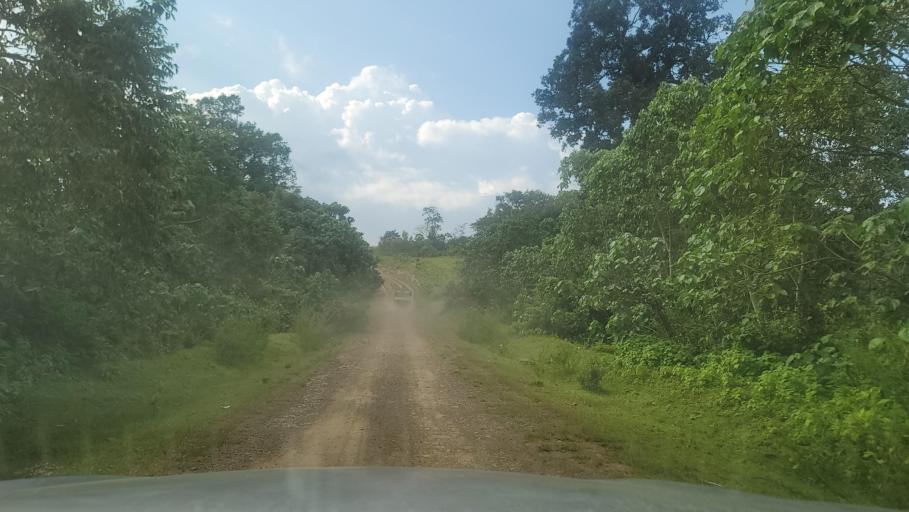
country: ET
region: Southern Nations, Nationalities, and People's Region
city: Bonga
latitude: 7.5773
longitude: 36.1609
